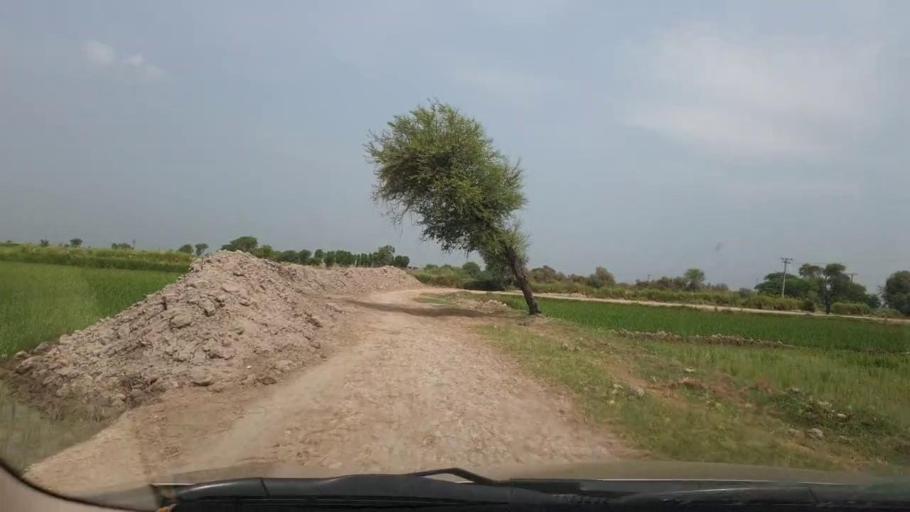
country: PK
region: Sindh
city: Goth Garelo
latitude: 27.5208
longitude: 68.1216
